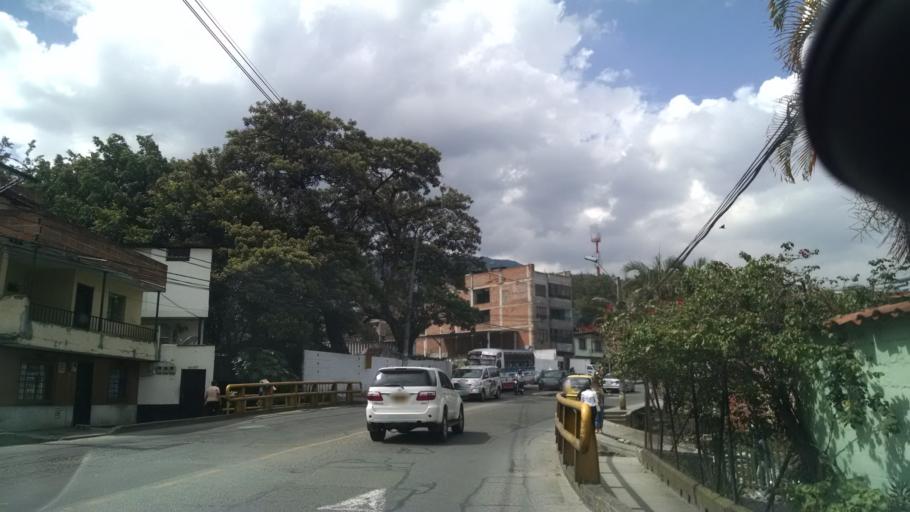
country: CO
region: Antioquia
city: Medellin
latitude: 6.2723
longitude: -75.5797
